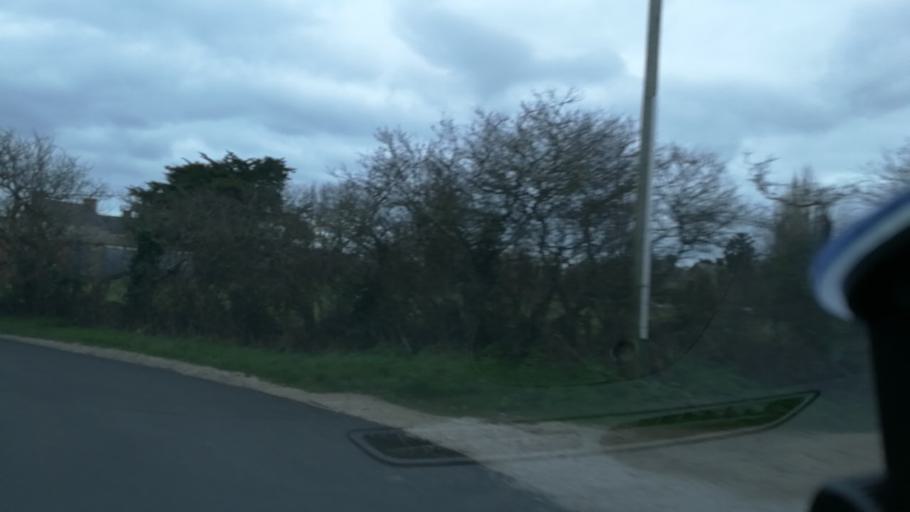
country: FR
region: Lower Normandy
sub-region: Departement de la Manche
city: Fermanville
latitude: 49.6834
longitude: -1.4567
